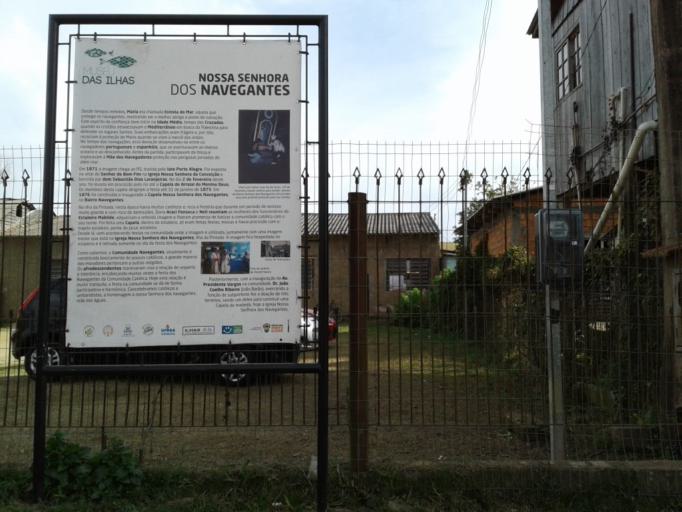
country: BR
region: Rio Grande do Sul
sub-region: Porto Alegre
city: Porto Alegre
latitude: -30.0278
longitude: -51.2530
